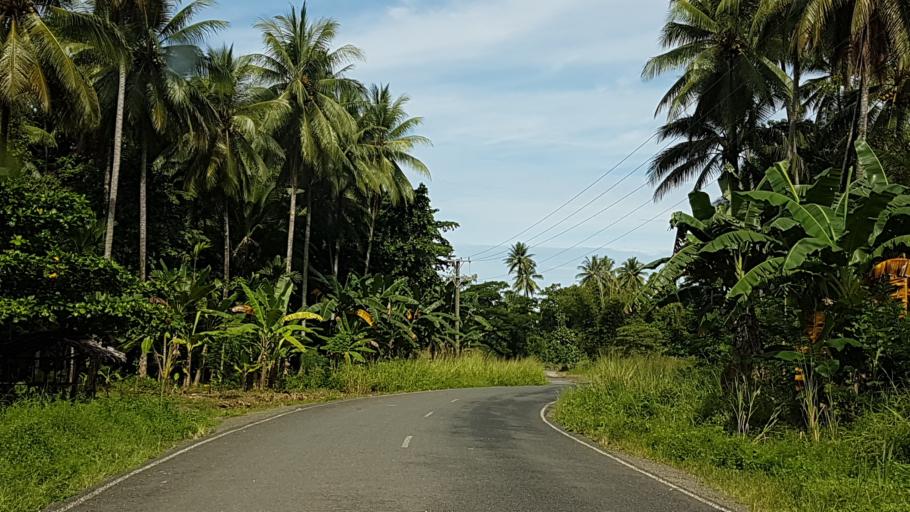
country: PG
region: Milne Bay
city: Alotau
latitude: -10.3231
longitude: 150.4811
